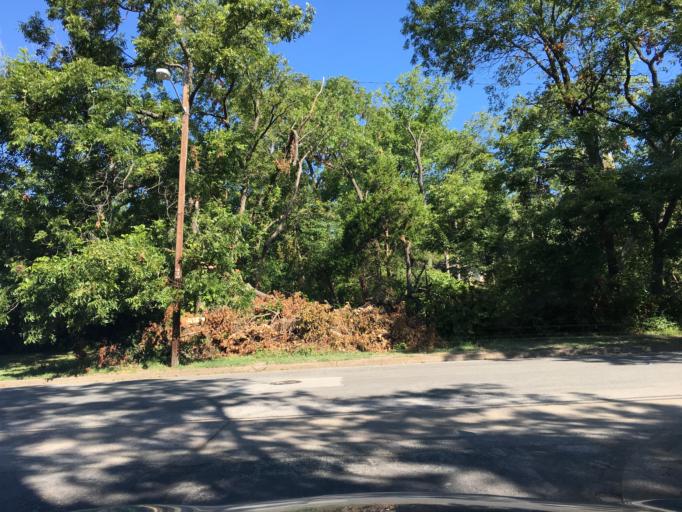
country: US
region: Texas
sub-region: Dallas County
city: Garland
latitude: 32.8568
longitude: -96.6973
